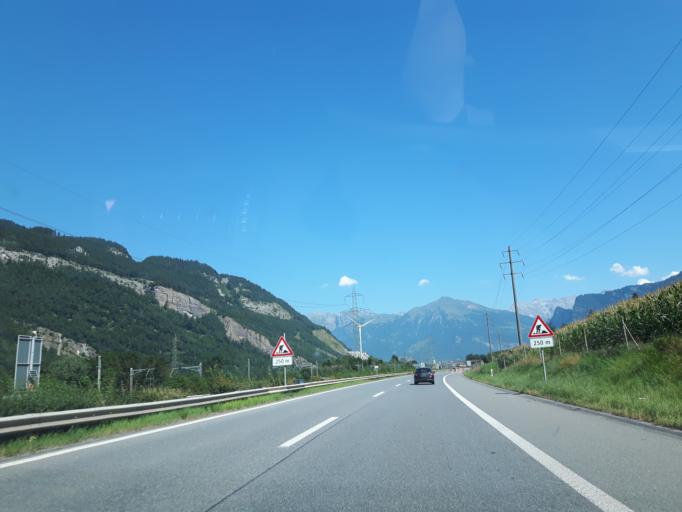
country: CH
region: Grisons
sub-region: Landquart District
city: Trimmis
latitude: 46.8820
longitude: 9.5353
